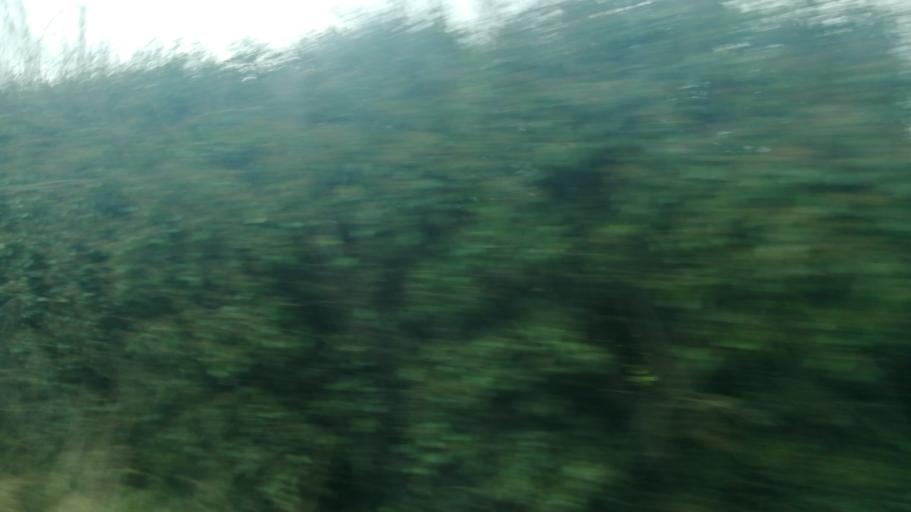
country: IE
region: Leinster
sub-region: Kildare
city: Clane
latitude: 53.3197
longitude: -6.7036
